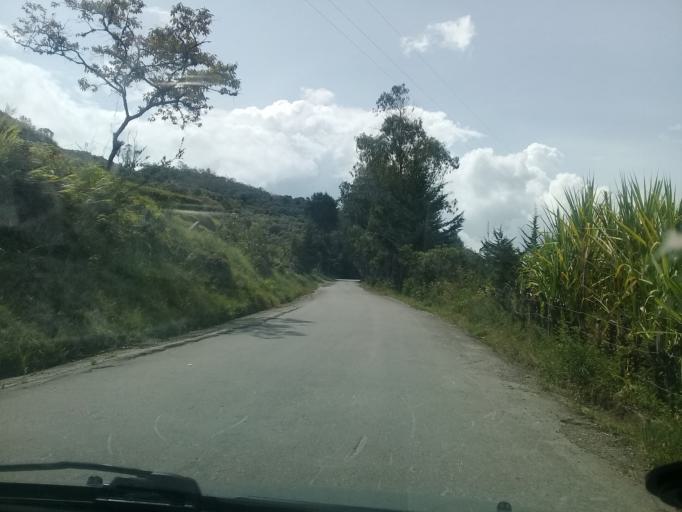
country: CO
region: Cundinamarca
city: Gachala
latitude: 4.6993
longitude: -73.4829
